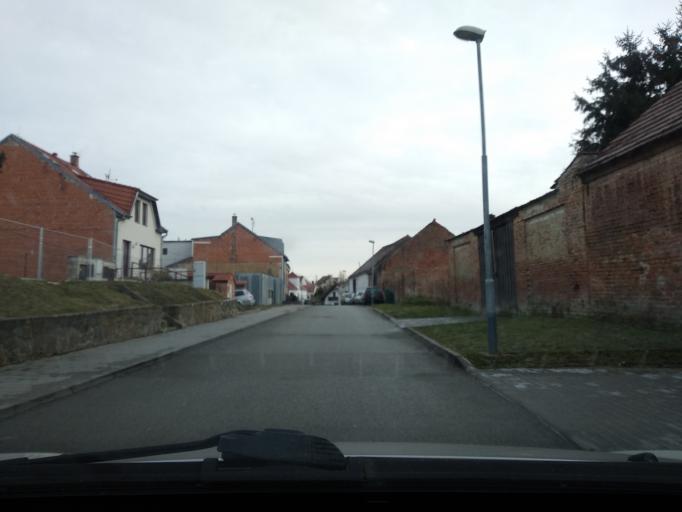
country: CZ
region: South Moravian
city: Ostopovice
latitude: 49.1655
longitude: 16.5625
